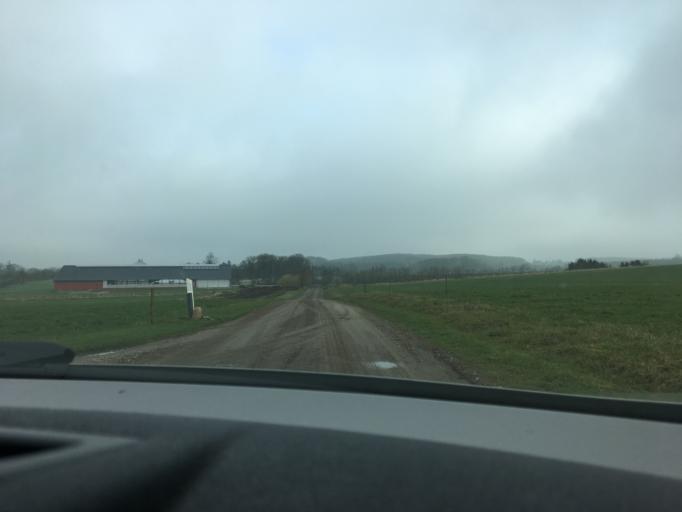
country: DK
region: South Denmark
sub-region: Vejle Kommune
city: Give
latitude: 55.8205
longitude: 9.2994
